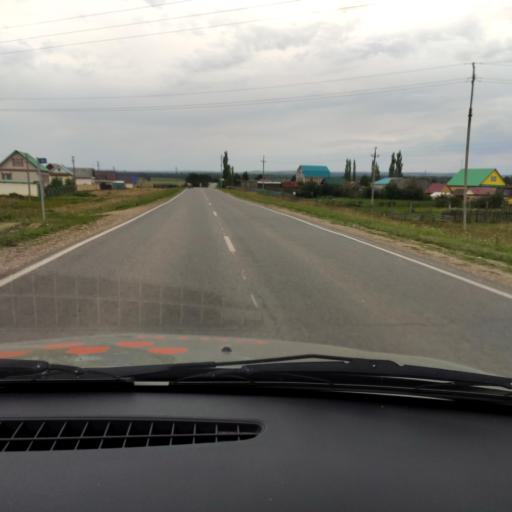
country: RU
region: Bashkortostan
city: Krasnaya Gorka
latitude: 55.1833
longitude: 56.6782
